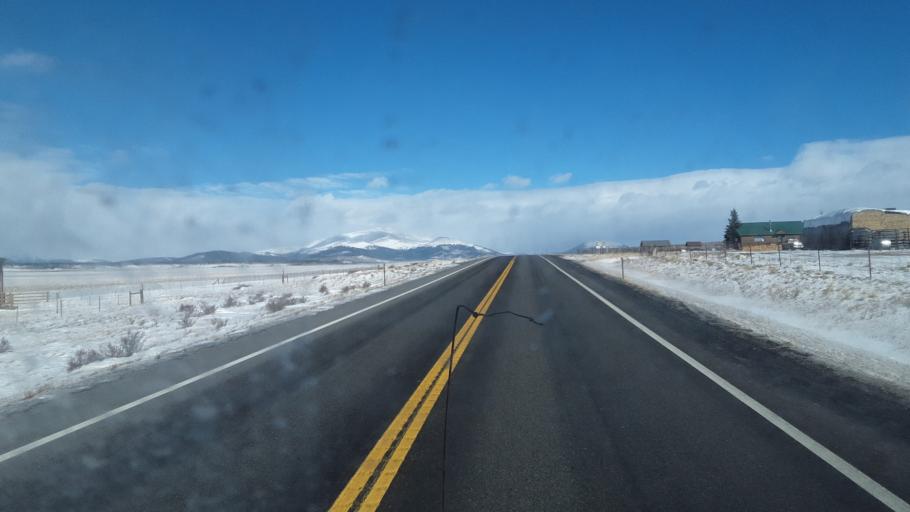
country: US
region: Colorado
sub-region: Park County
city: Fairplay
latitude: 39.1757
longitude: -106.0006
